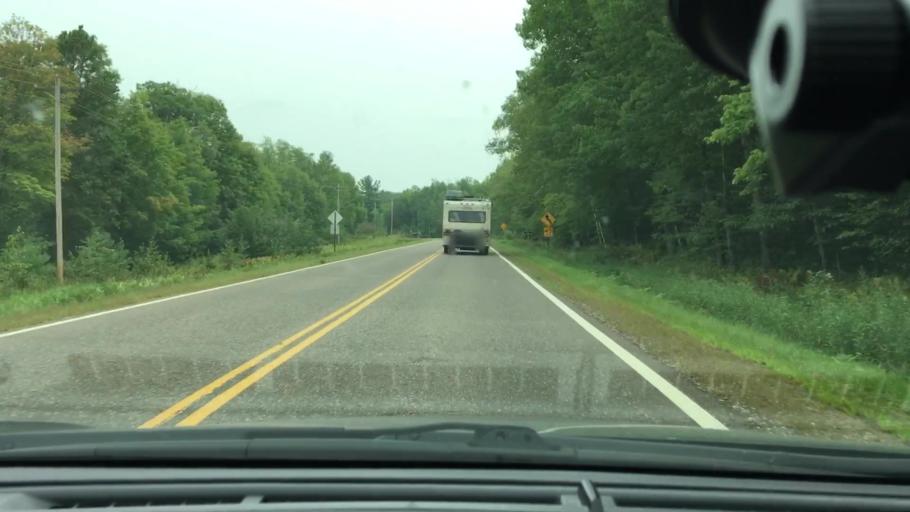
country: US
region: Minnesota
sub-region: Aitkin County
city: Aitkin
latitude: 46.4022
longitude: -93.7975
